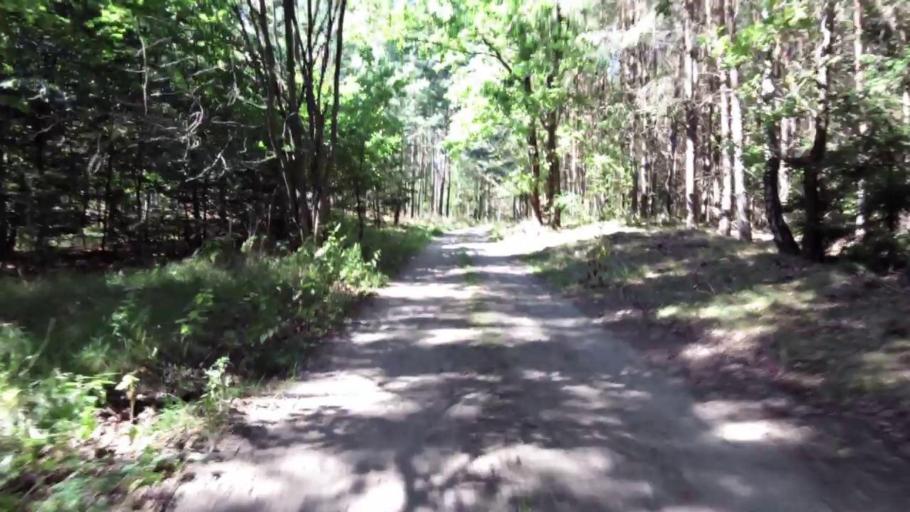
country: PL
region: West Pomeranian Voivodeship
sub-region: Powiat szczecinecki
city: Borne Sulinowo
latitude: 53.6635
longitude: 16.5636
